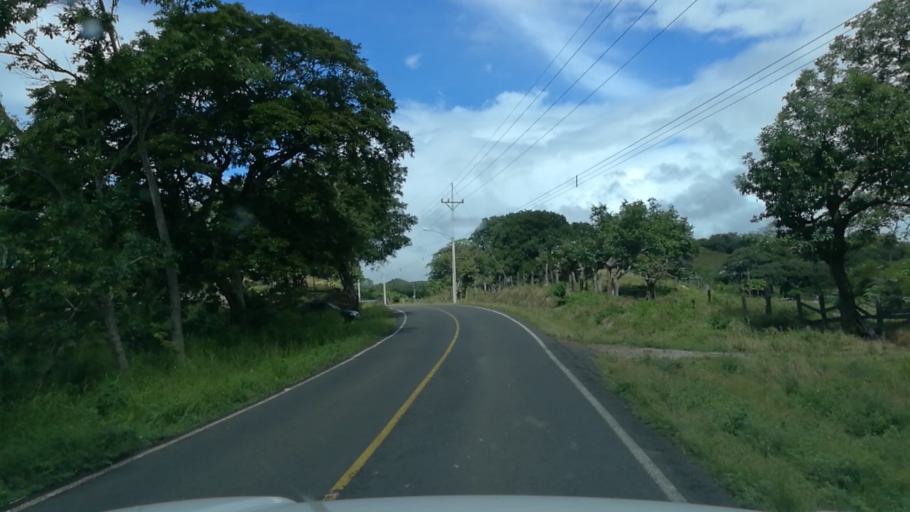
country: CR
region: Guanacaste
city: Fortuna
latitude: 10.6467
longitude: -85.2327
